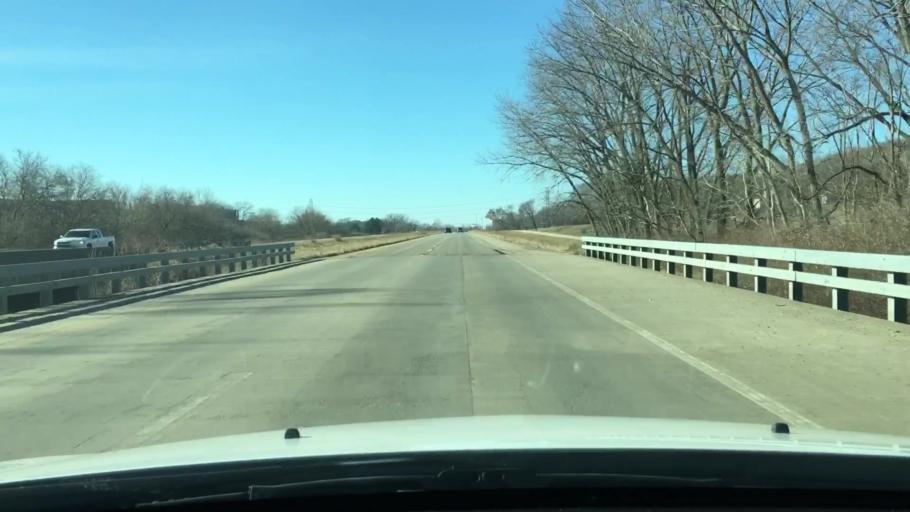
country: US
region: Illinois
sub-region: Peoria County
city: Glasford
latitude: 40.5630
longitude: -89.7435
